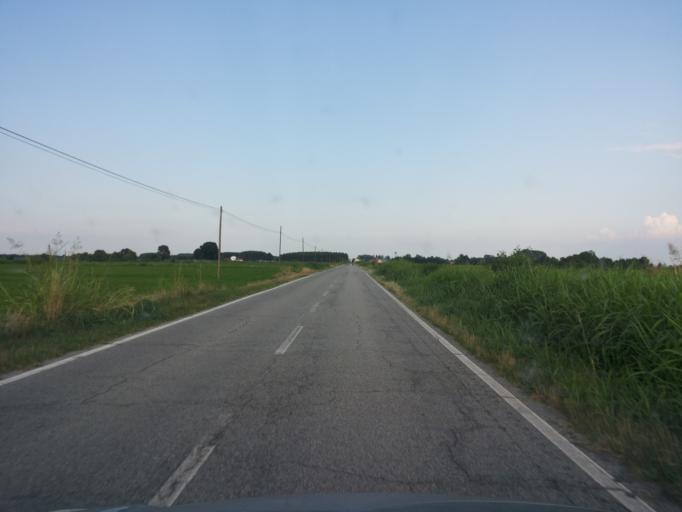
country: IT
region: Piedmont
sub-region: Provincia di Vercelli
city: Asigliano Vercellese
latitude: 45.2650
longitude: 8.3844
